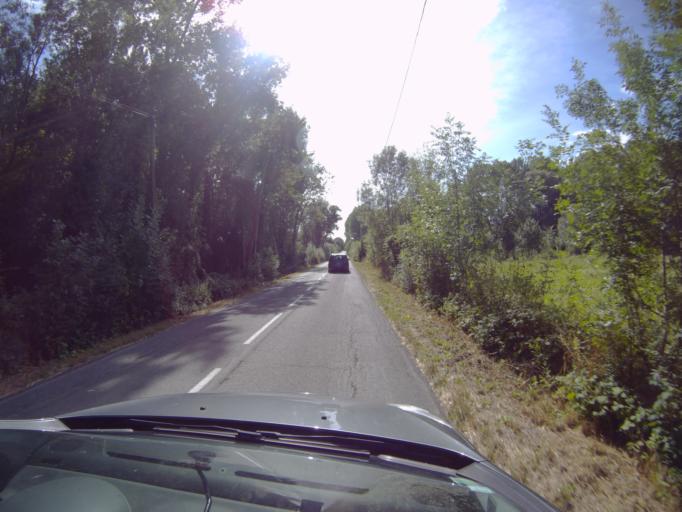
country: FR
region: Poitou-Charentes
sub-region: Departement des Deux-Sevres
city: Saint-Hilaire-la-Palud
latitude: 46.2536
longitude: -0.7499
